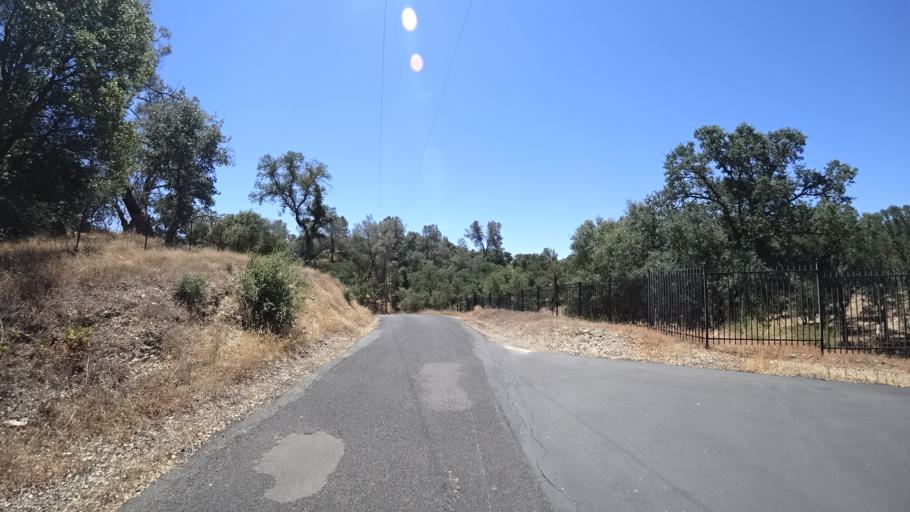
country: US
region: California
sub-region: Calaveras County
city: Copperopolis
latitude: 37.9757
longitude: -120.6947
